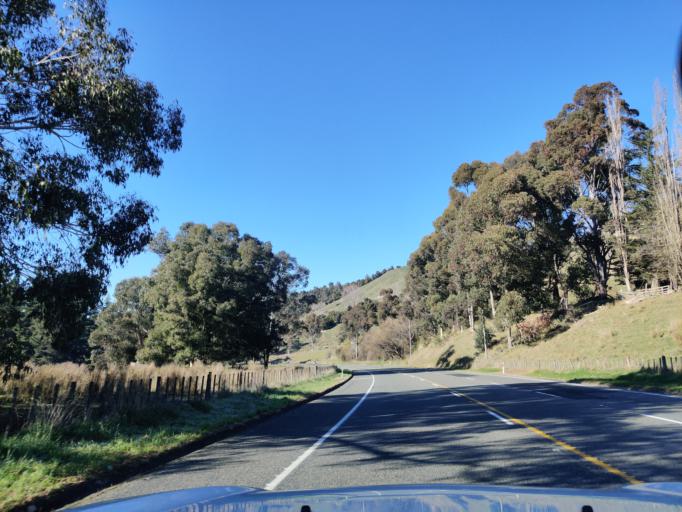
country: NZ
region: Manawatu-Wanganui
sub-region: Ruapehu District
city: Waiouru
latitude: -39.7932
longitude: 175.7853
